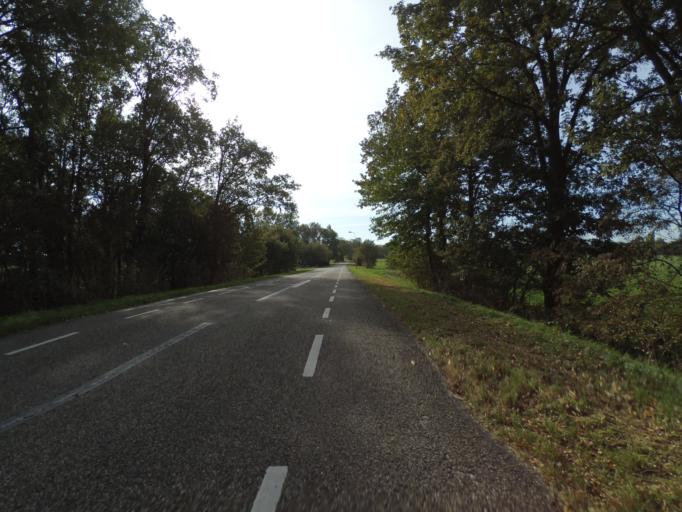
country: NL
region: Gelderland
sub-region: Gemeente Lochem
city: Laren
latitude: 52.2466
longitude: 6.3891
